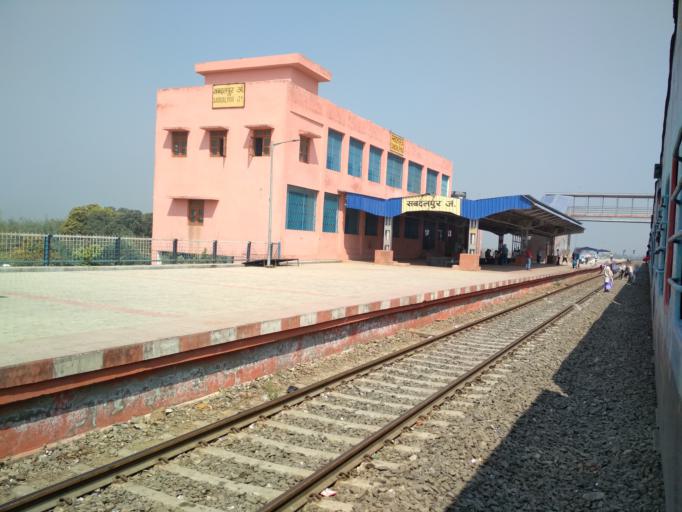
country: IN
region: Bihar
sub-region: Munger
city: Munger
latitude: 25.4273
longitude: 86.4388
